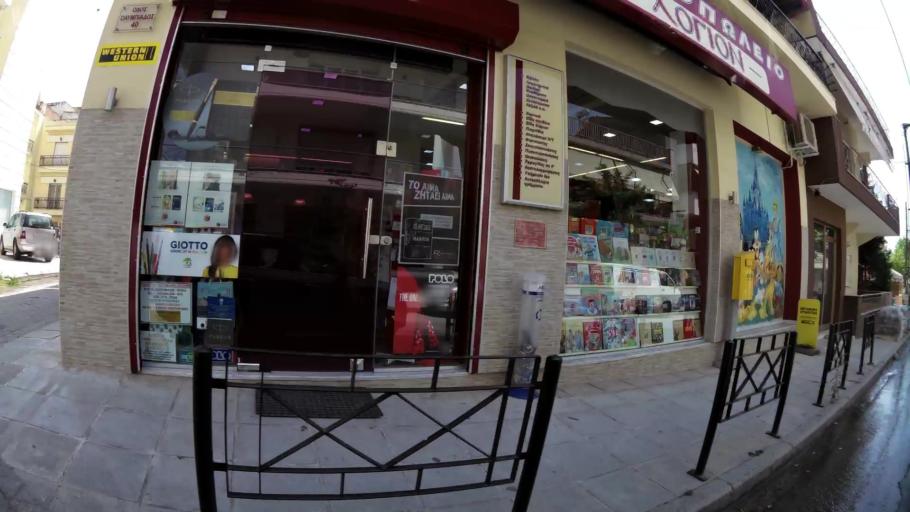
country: GR
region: Central Macedonia
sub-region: Nomos Thessalonikis
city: Evosmos
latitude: 40.6702
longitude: 22.9157
